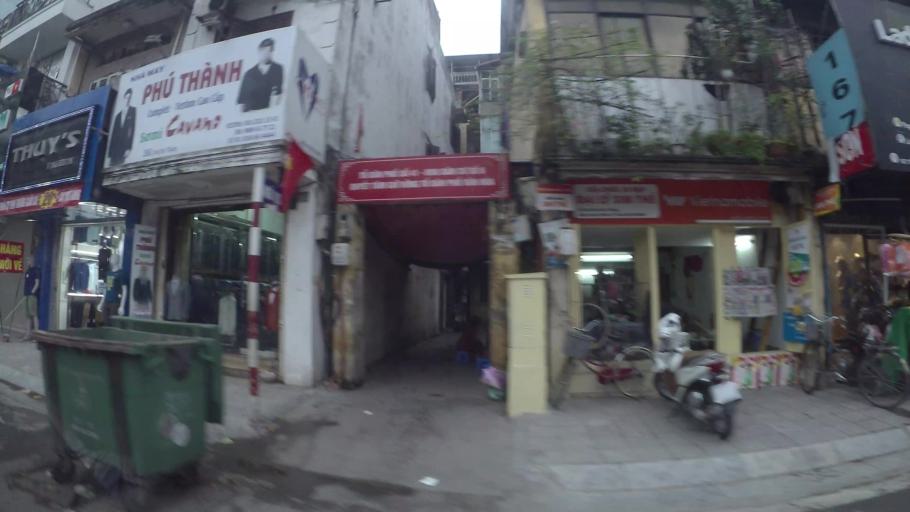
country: VN
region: Ha Noi
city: Dong Da
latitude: 21.0226
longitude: 105.8319
